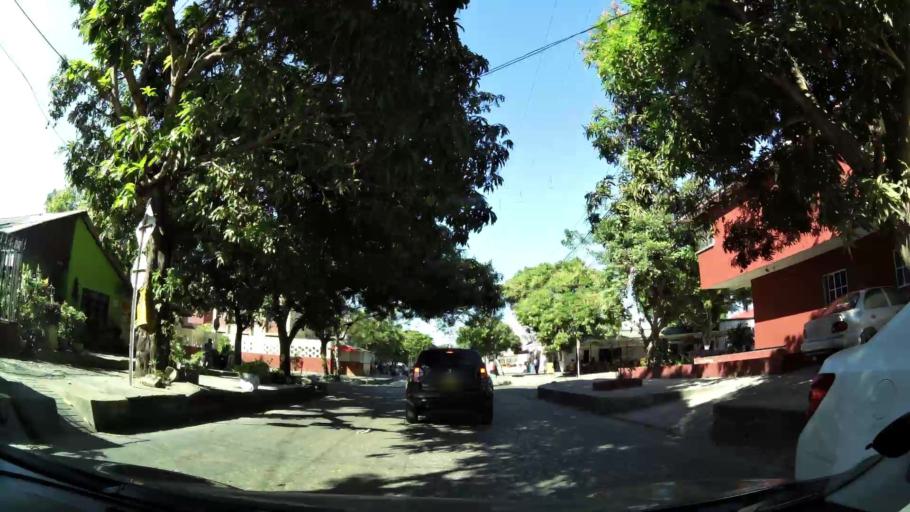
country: CO
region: Atlantico
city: Barranquilla
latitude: 10.9517
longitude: -74.7915
